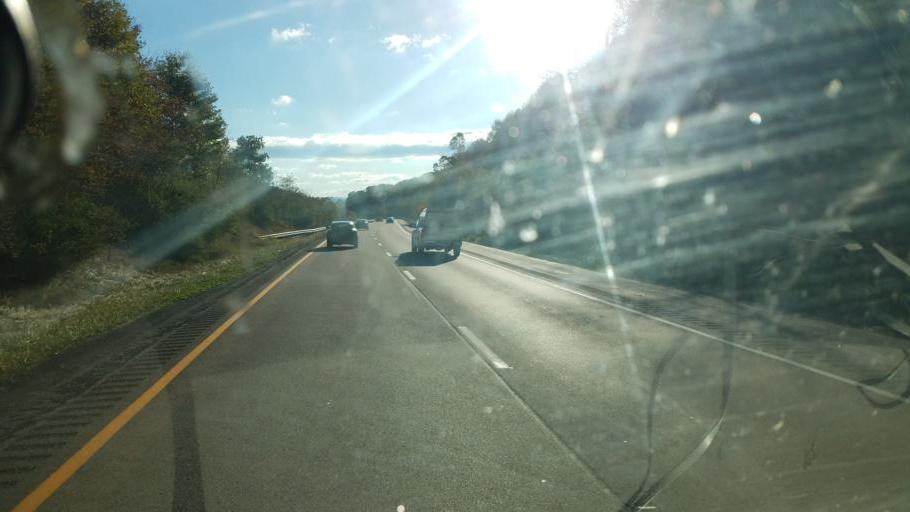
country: US
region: Maryland
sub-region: Allegany County
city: Frostburg
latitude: 39.6410
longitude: -78.8827
